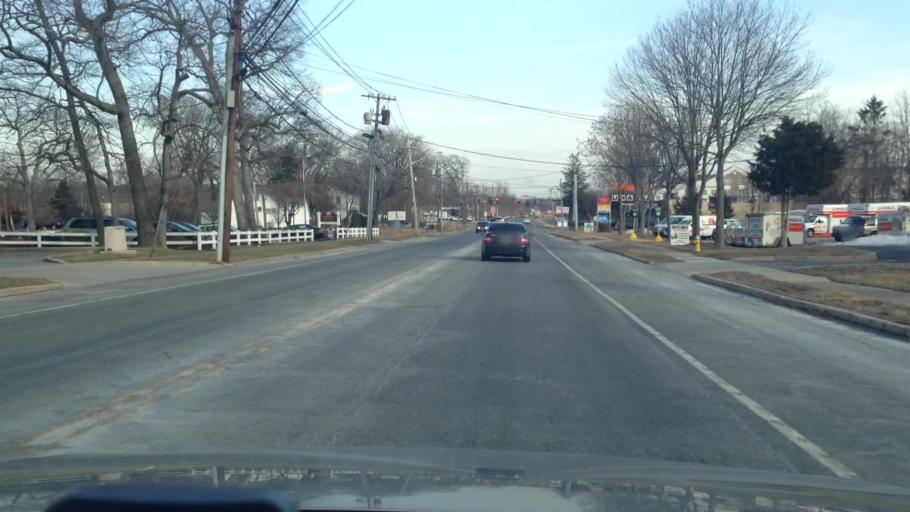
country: US
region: New York
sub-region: Suffolk County
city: Coram
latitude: 40.8687
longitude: -73.0123
